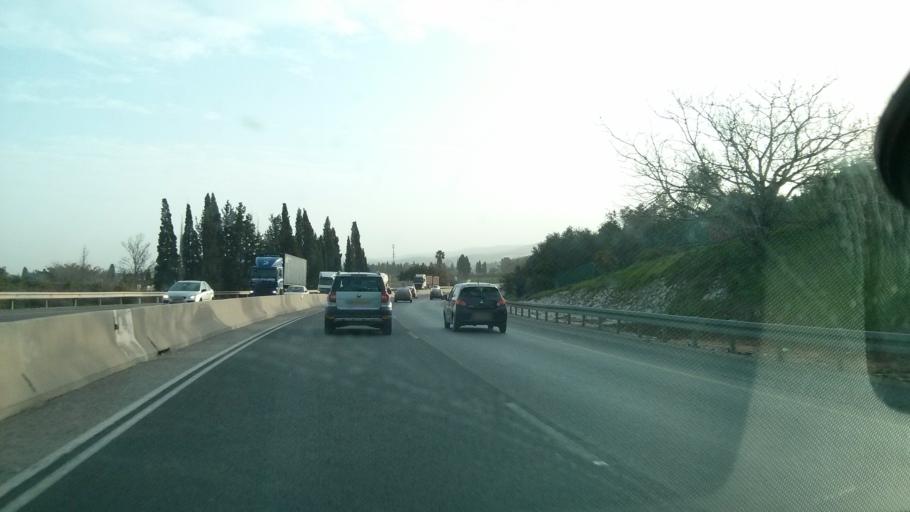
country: PS
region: West Bank
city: Nazlat `Isa
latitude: 32.4686
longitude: 34.9986
